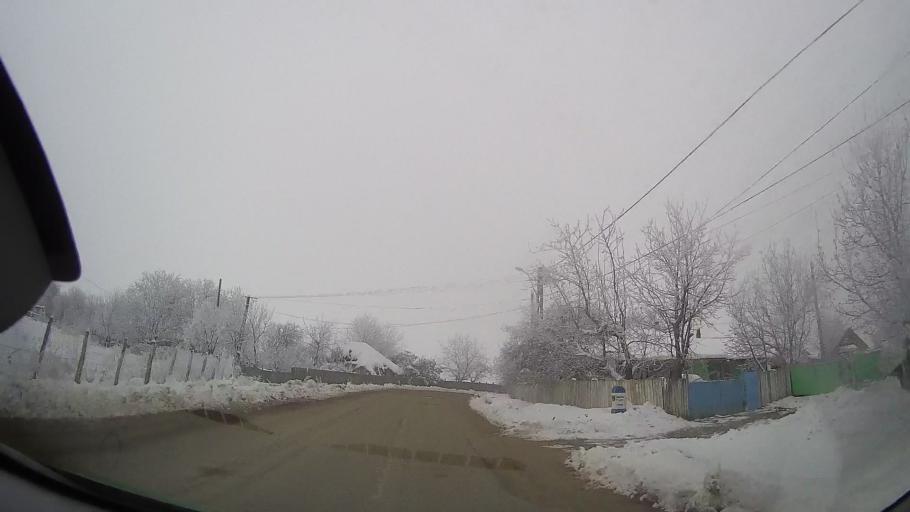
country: RO
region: Iasi
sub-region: Comuna Tansa
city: Tansa
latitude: 46.9098
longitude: 27.2261
